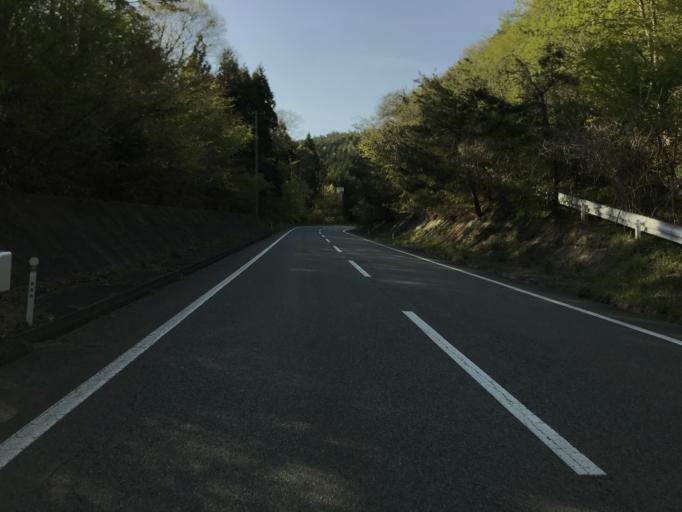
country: JP
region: Fukushima
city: Funehikimachi-funehiki
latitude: 37.5303
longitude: 140.7473
